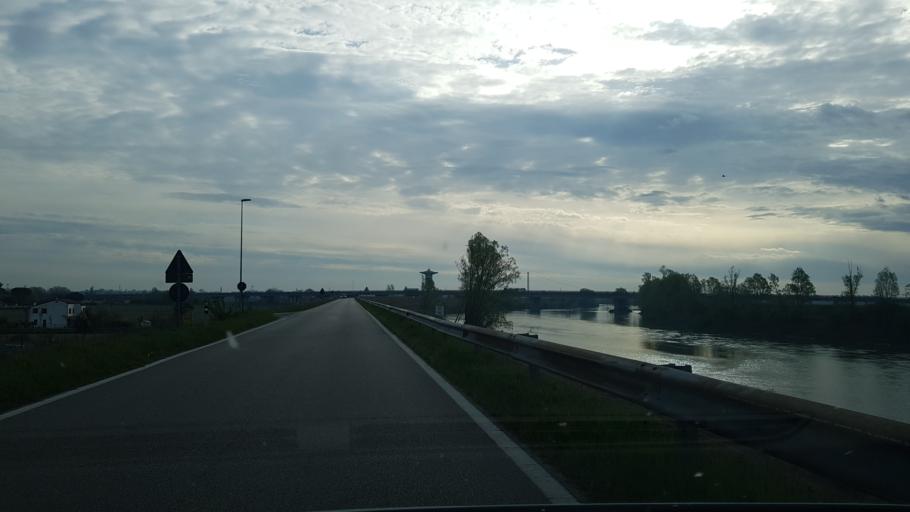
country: IT
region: Veneto
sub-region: Provincia di Padova
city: Barbona
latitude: 45.0975
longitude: 11.7437
